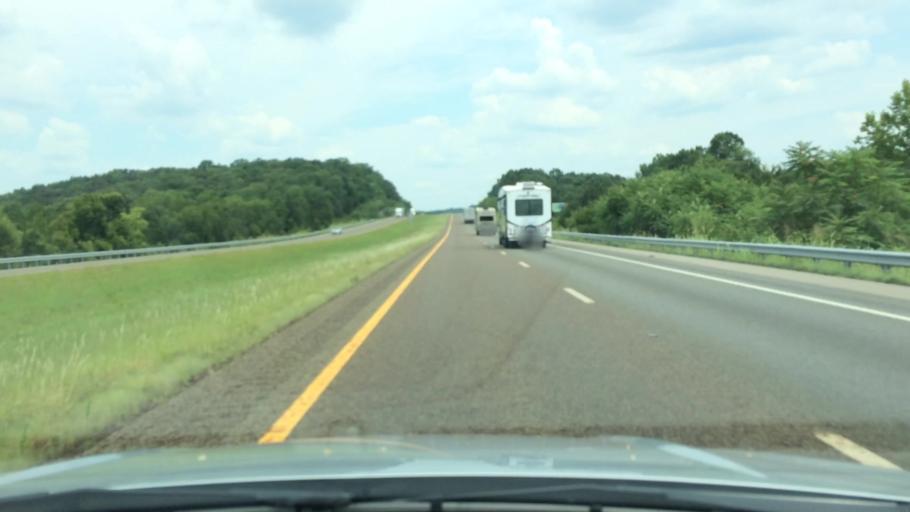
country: US
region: Tennessee
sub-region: Maury County
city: Columbia
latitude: 35.6049
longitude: -86.9011
